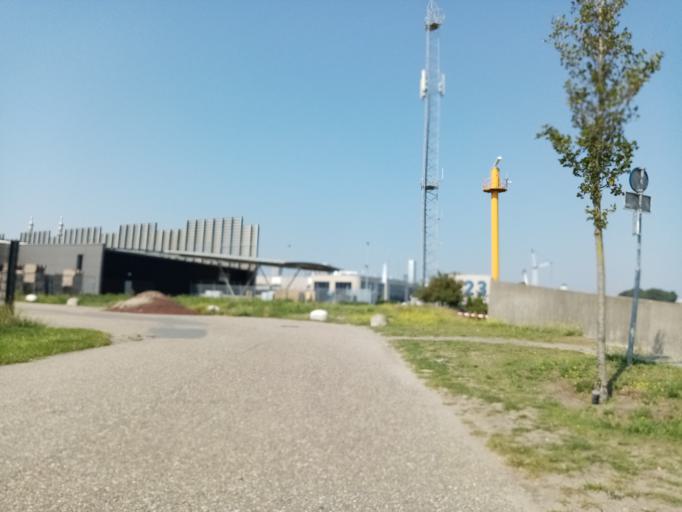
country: NL
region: South Holland
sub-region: Gemeente Rotterdam
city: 's-Gravenland
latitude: 51.8990
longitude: 4.5193
